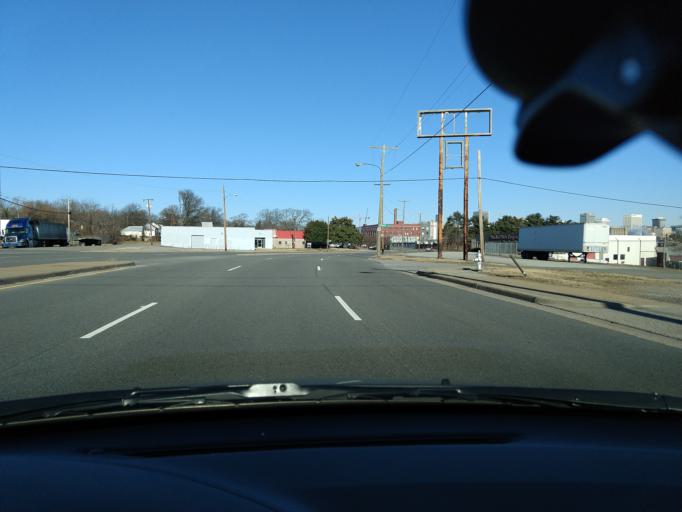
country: US
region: Virginia
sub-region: City of Richmond
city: Richmond
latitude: 37.5171
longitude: -77.4368
